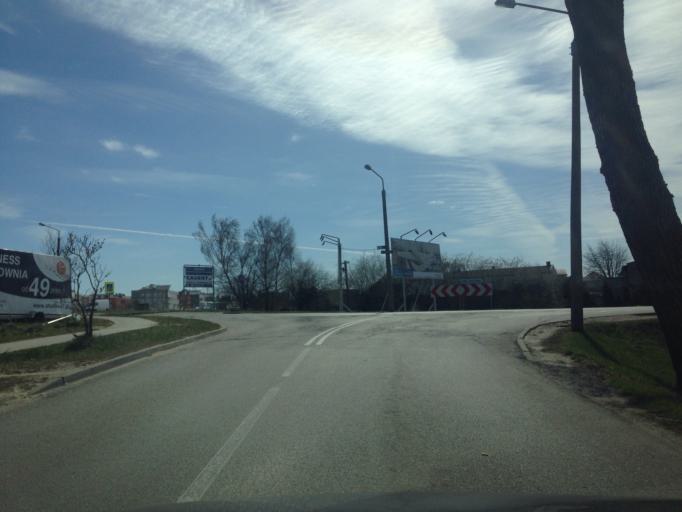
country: PL
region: Pomeranian Voivodeship
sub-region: Powiat wejherowski
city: Bojano
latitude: 54.4906
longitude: 18.4248
